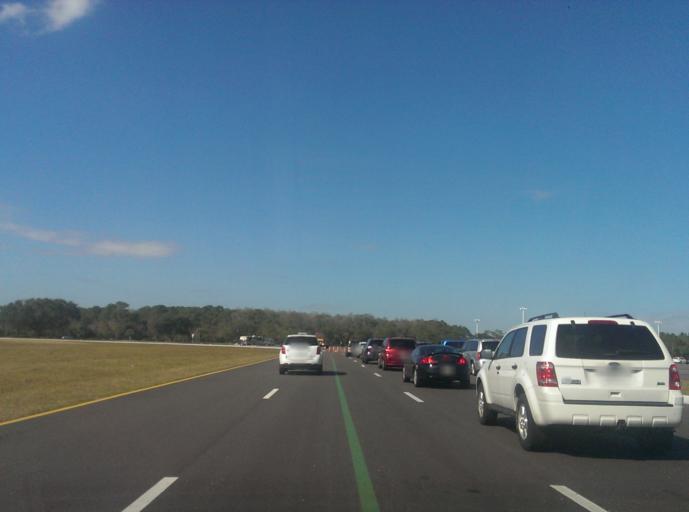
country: US
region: Florida
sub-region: Osceola County
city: Celebration
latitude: 28.3975
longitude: -81.5788
